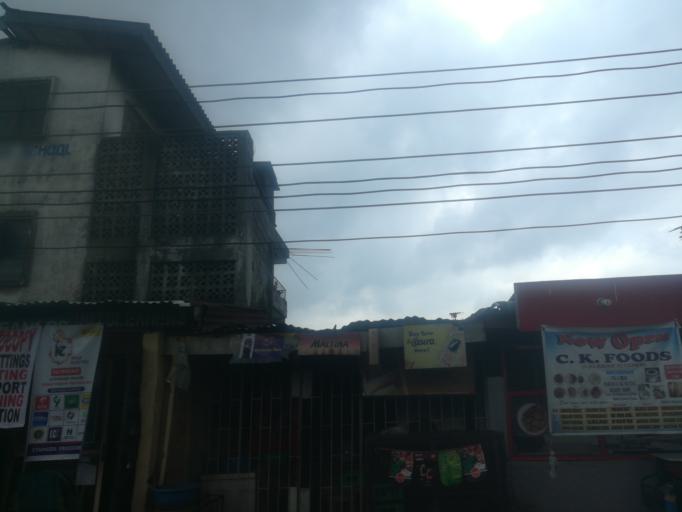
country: NG
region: Lagos
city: Ojota
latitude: 6.5945
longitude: 3.3858
